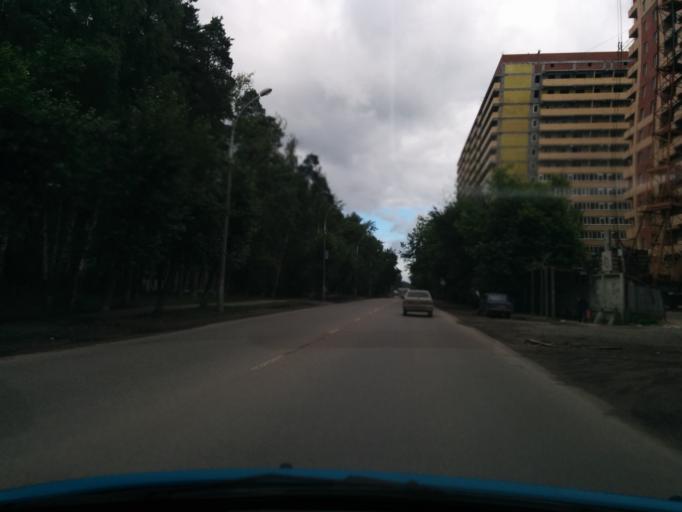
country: RU
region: Perm
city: Kondratovo
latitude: 58.0298
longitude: 56.0179
